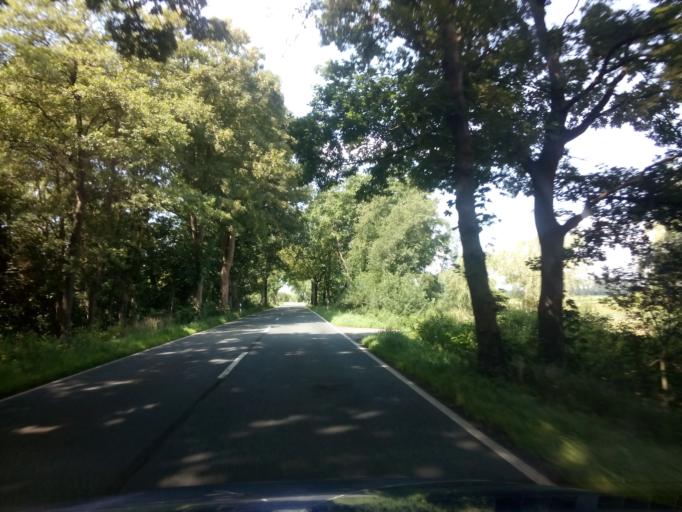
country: DE
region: Lower Saxony
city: Worpswede
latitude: 53.2607
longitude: 8.9306
